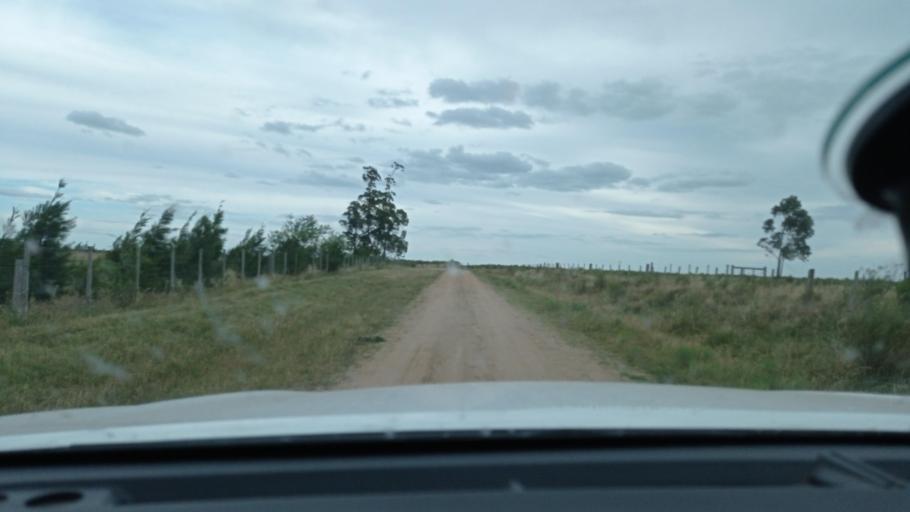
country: UY
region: Florida
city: Casupa
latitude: -34.1225
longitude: -55.8153
